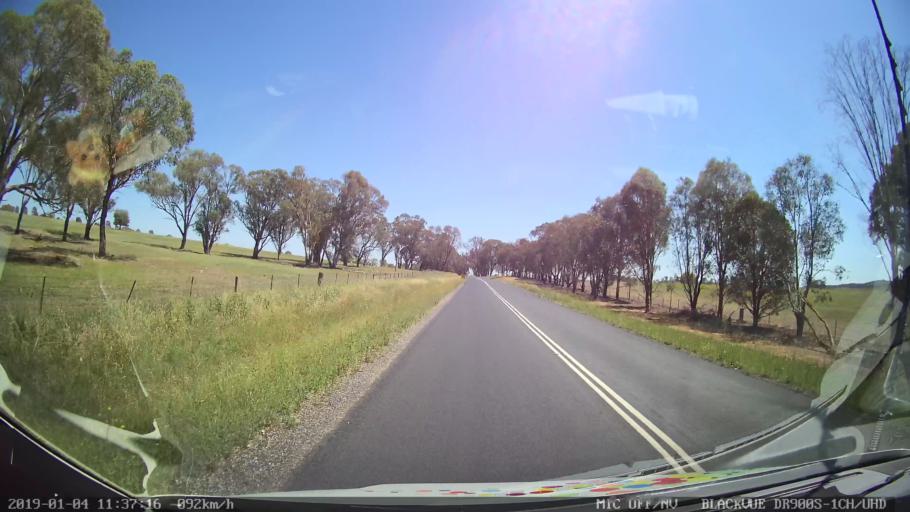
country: AU
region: New South Wales
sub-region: Cabonne
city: Molong
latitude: -33.0345
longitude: 148.8084
